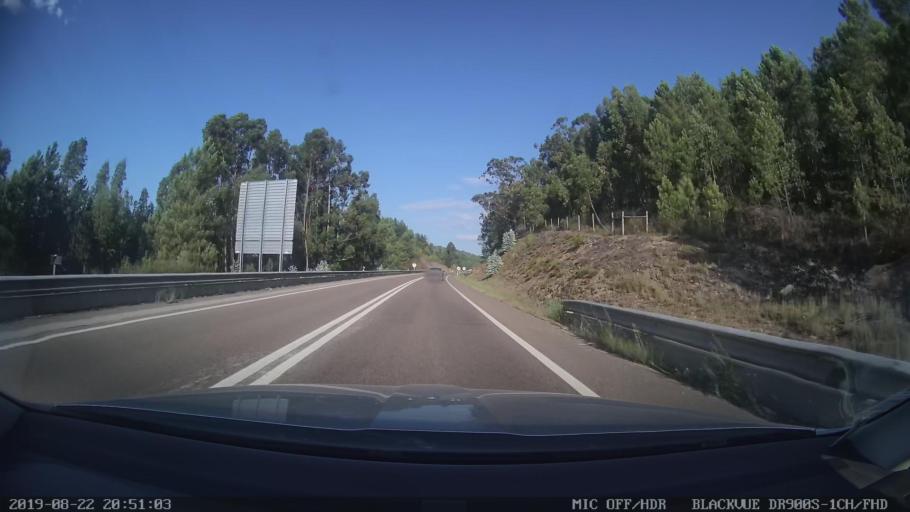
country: PT
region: Castelo Branco
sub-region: Proenca-A-Nova
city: Proenca-a-Nova
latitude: 39.7583
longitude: -7.9514
